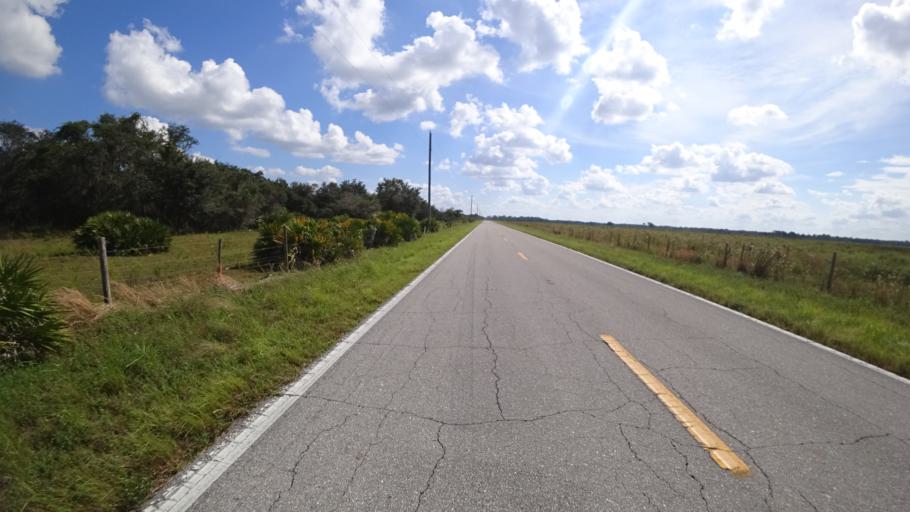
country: US
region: Florida
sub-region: Hardee County
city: Wauchula
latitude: 27.5093
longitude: -82.0720
